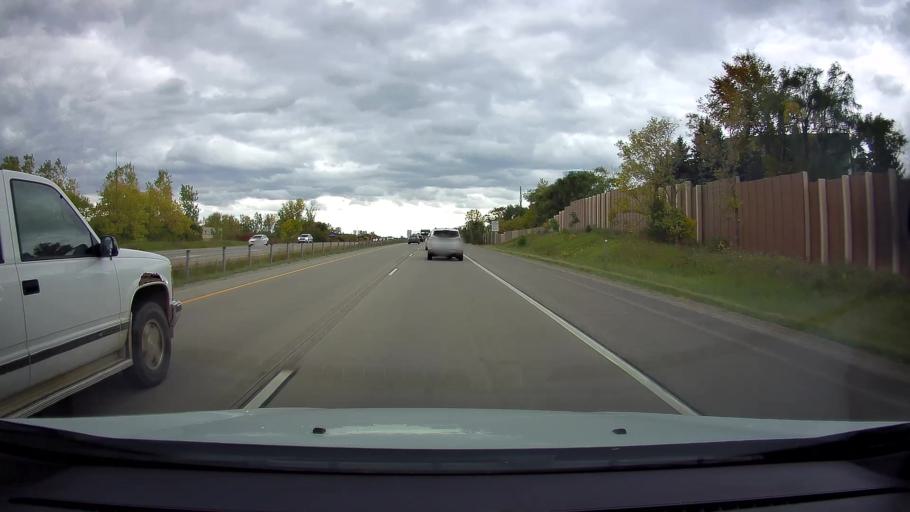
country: US
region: Minnesota
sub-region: Ramsey County
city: North Oaks
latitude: 45.0855
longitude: -93.0529
